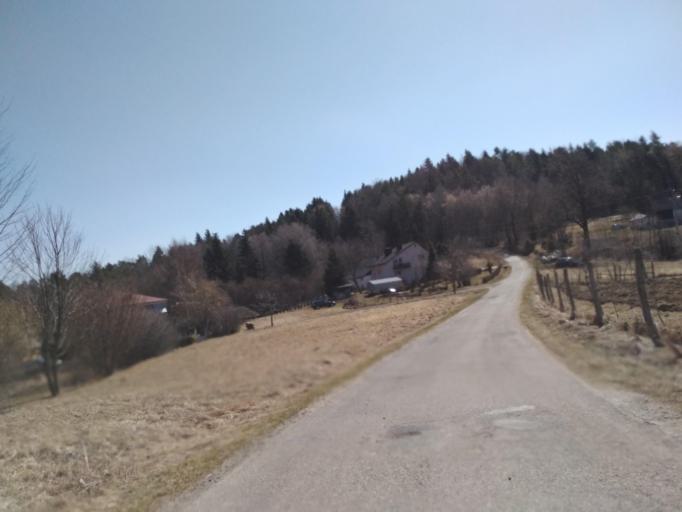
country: PL
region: Subcarpathian Voivodeship
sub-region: Powiat brzozowski
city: Jablonica Polska
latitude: 49.7351
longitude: 21.8998
